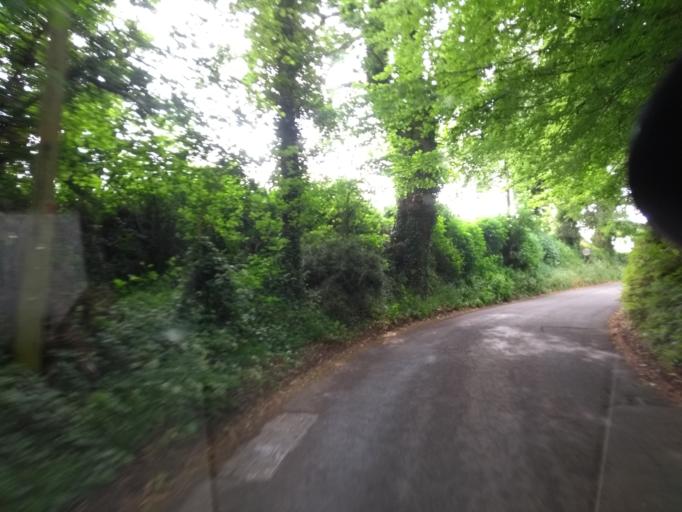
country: GB
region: England
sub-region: Somerset
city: Bishops Lydeard
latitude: 51.1257
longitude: -3.1171
